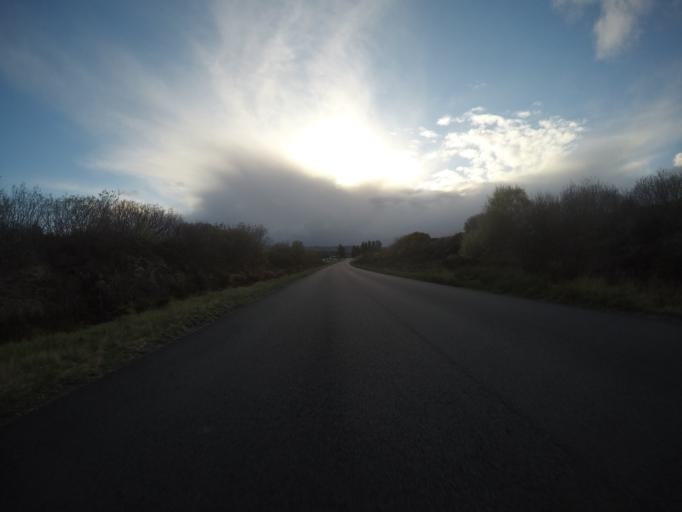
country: GB
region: Scotland
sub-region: Highland
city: Portree
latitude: 57.4508
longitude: -6.2795
